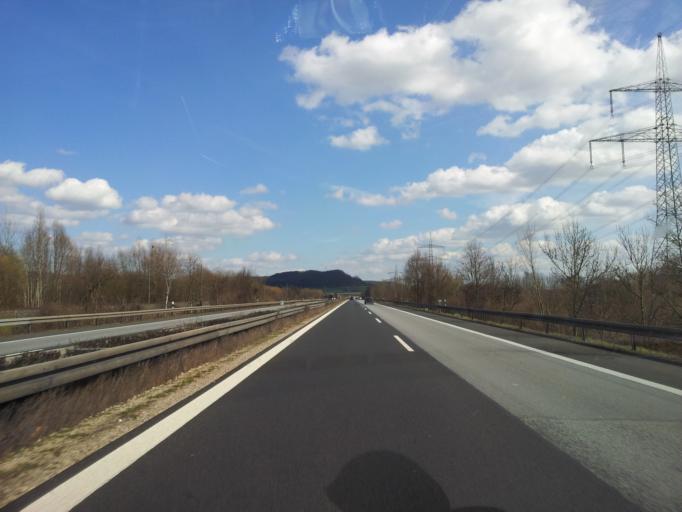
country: DE
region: Bavaria
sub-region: Regierungsbezirk Unterfranken
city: Stettfeld
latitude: 49.9699
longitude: 10.7087
